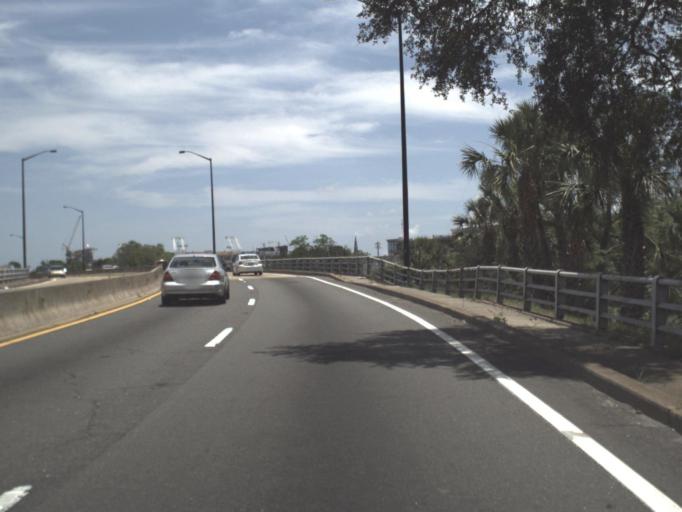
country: US
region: Florida
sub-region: Duval County
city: Jacksonville
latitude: 30.3300
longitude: -81.6488
